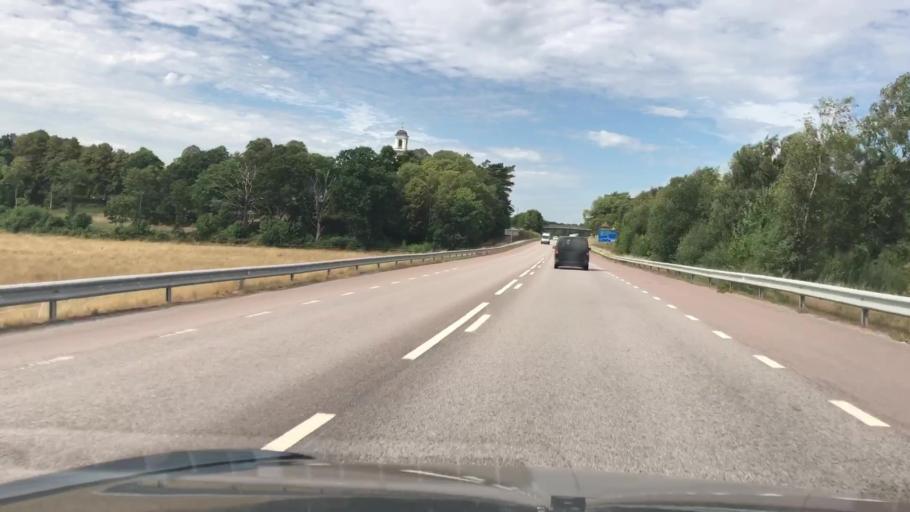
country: SE
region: Blekinge
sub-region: Karlskrona Kommun
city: Rodeby
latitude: 56.1969
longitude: 15.6935
